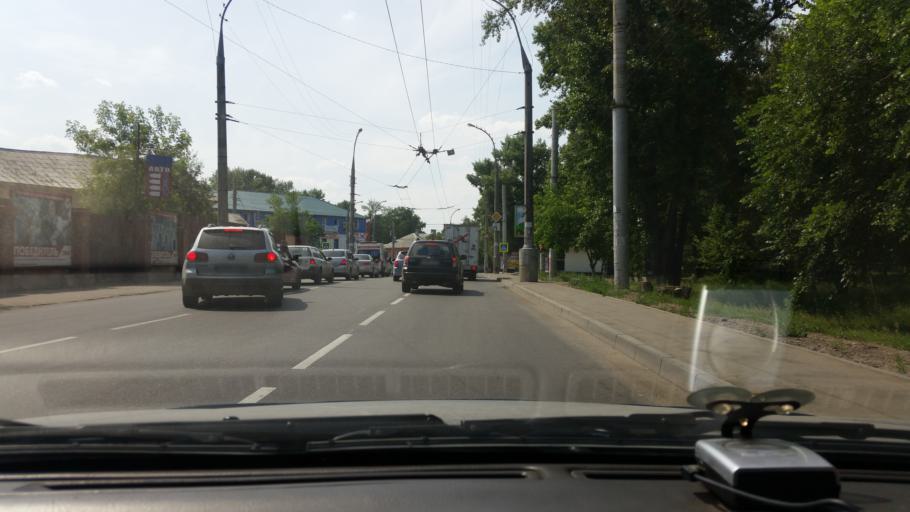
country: RU
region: Irkutsk
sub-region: Irkutskiy Rayon
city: Irkutsk
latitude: 52.2295
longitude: 104.3103
